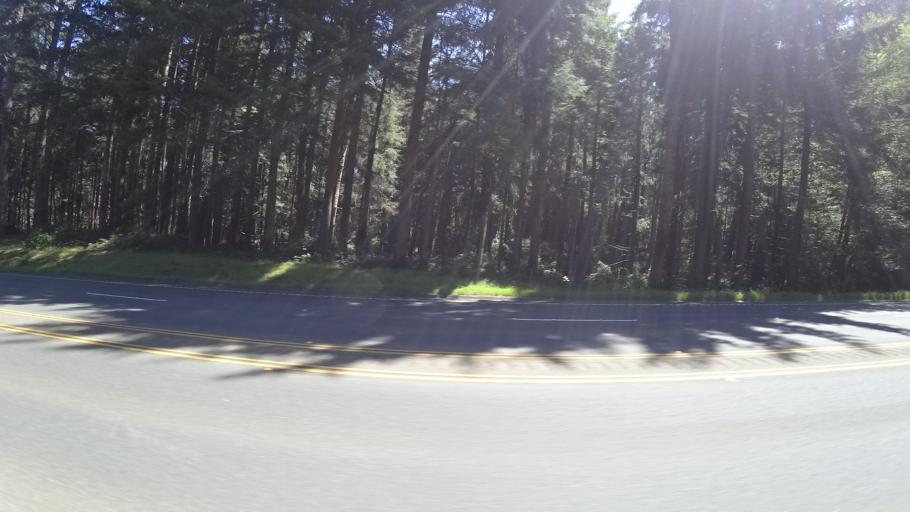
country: US
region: California
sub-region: Humboldt County
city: Westhaven-Moonstone
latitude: 41.1477
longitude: -124.1361
